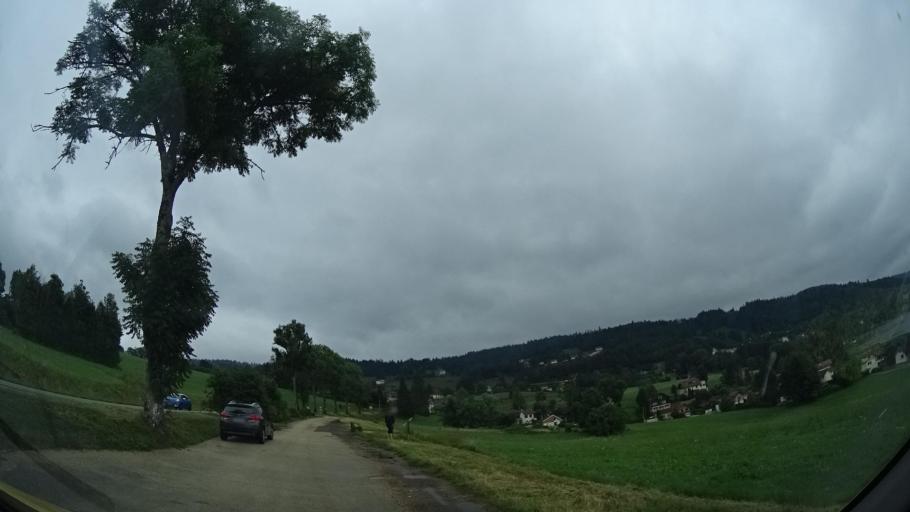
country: FR
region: Franche-Comte
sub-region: Departement du Doubs
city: Les Fourgs
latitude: 46.8387
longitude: 6.3401
